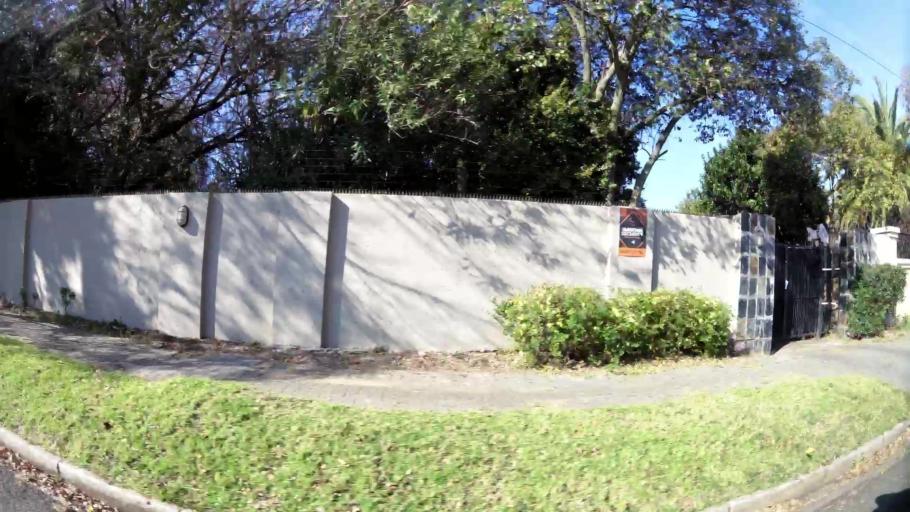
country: ZA
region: Gauteng
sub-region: City of Johannesburg Metropolitan Municipality
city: Johannesburg
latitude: -26.1729
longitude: 28.0789
